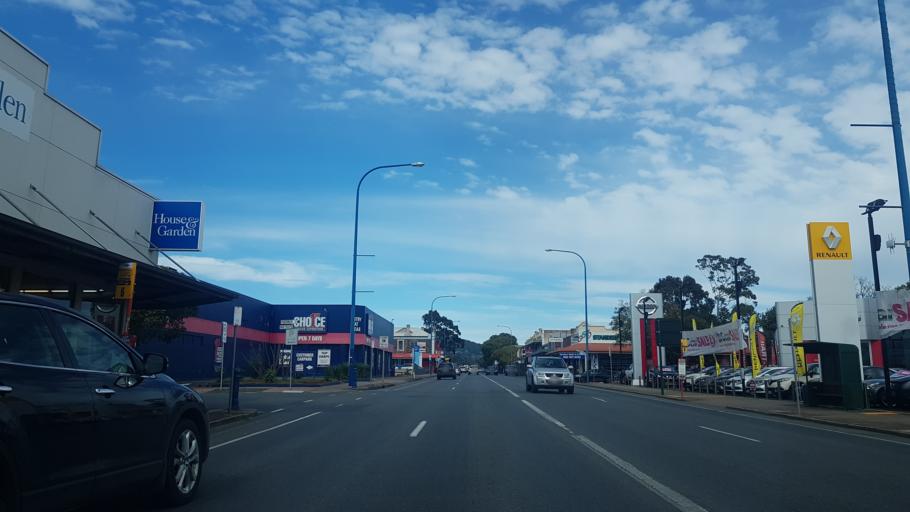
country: AU
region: South Australia
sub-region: Unley
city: Unley Park
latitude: -34.9554
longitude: 138.6079
